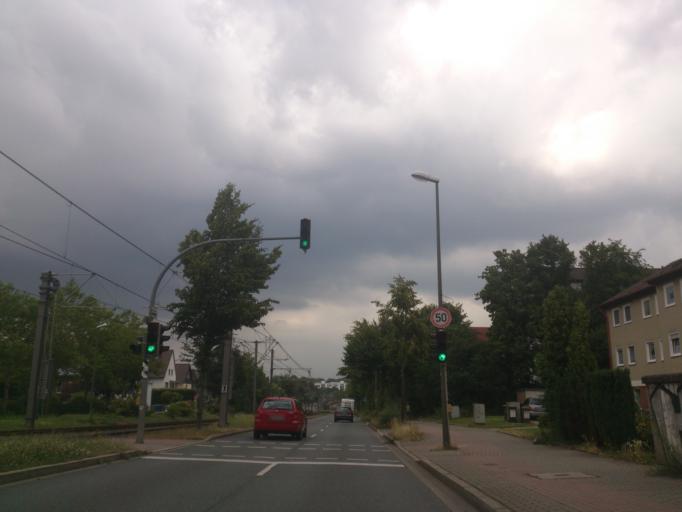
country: DE
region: North Rhine-Westphalia
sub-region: Regierungsbezirk Arnsberg
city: Dortmund
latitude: 51.4874
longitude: 7.4366
